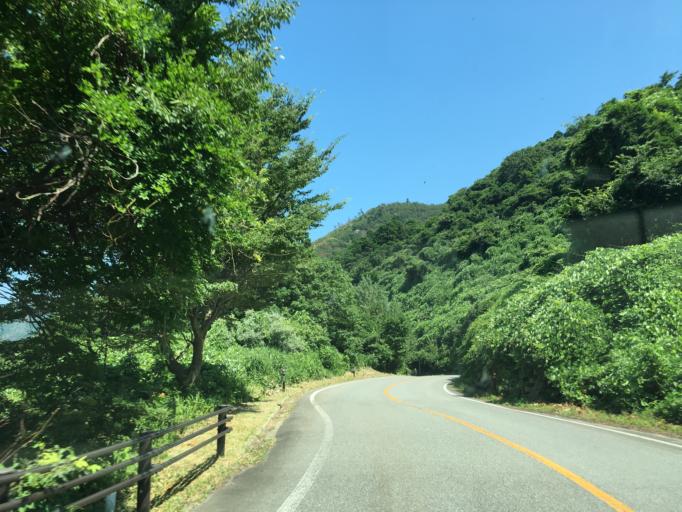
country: JP
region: Akita
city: Tenno
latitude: 39.9032
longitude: 139.7387
